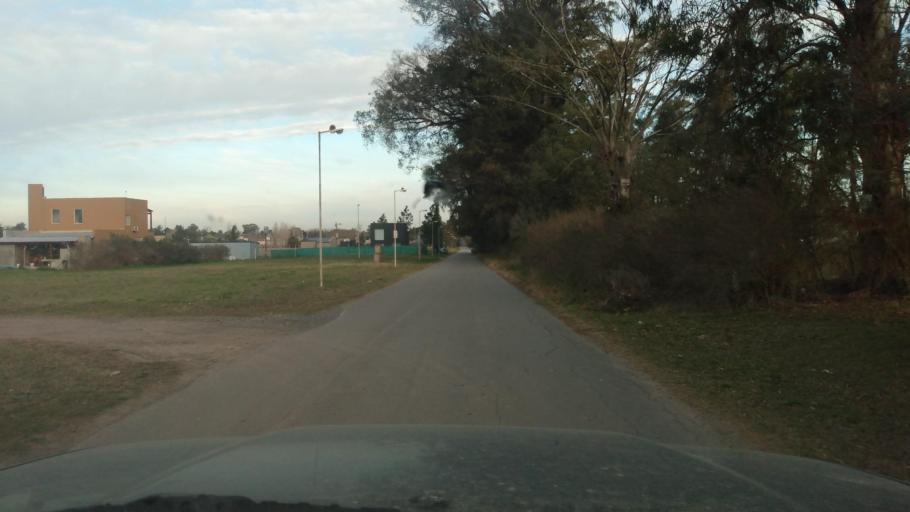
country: AR
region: Buenos Aires
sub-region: Partido de Lujan
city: Lujan
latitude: -34.5748
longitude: -59.0706
